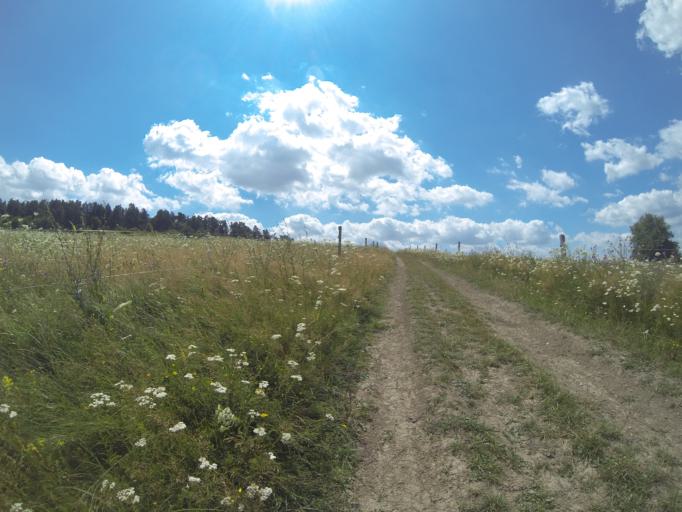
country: RO
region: Brasov
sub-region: Comuna Sercaia
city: Sercaia
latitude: 45.8681
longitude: 25.0941
